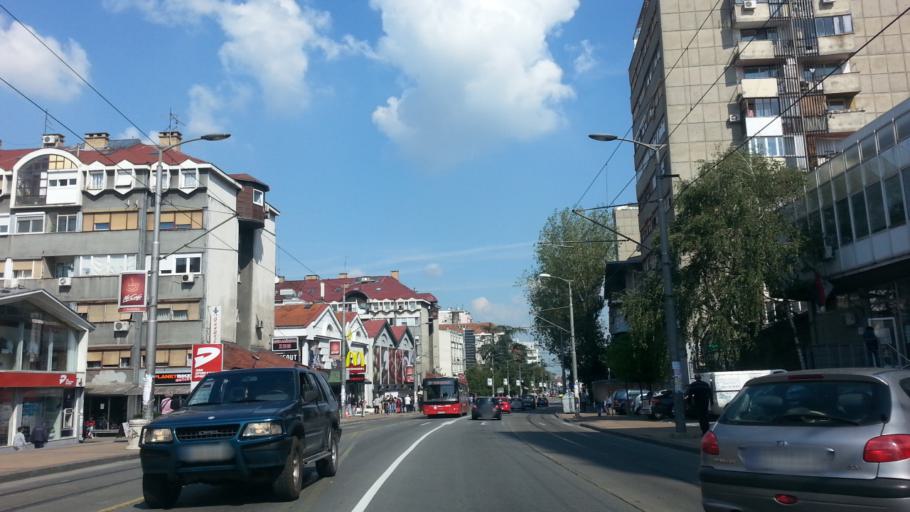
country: RS
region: Central Serbia
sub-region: Belgrade
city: Cukarica
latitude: 44.7768
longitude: 20.4140
